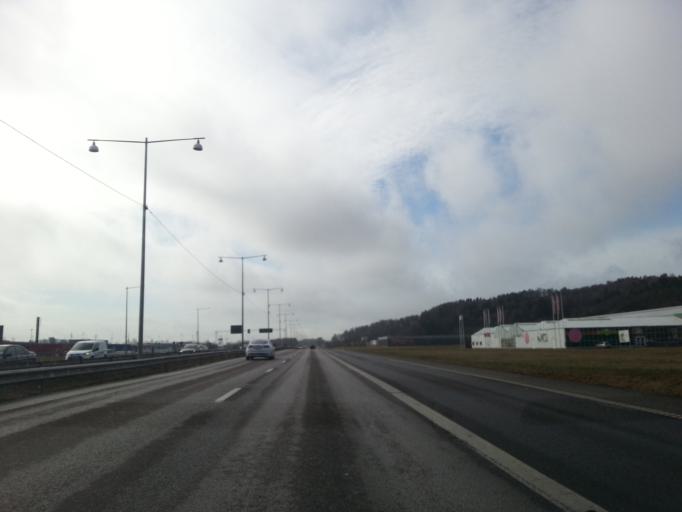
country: SE
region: Vaestra Goetaland
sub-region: Goteborg
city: Hammarkullen
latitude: 57.7737
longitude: 11.9969
